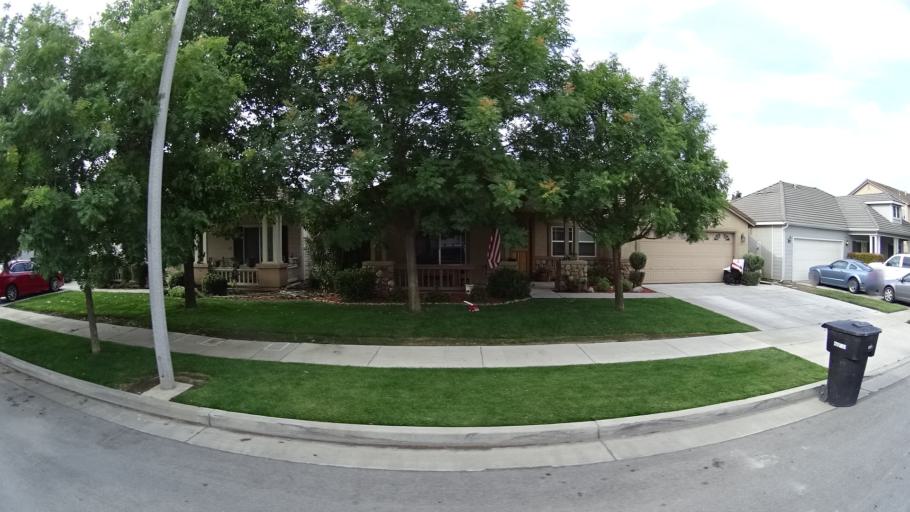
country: US
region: California
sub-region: Kings County
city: Hanford
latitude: 36.3349
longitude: -119.6786
